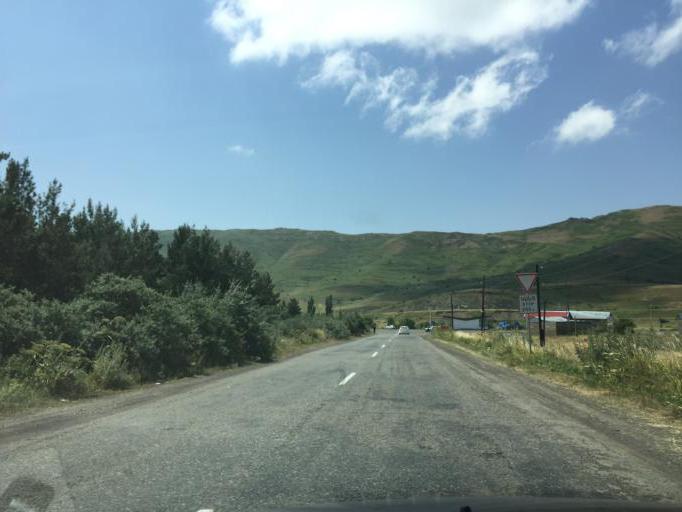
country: AM
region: Geghark'unik'i Marz
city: Tsovagyugh
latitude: 40.6111
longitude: 44.9563
